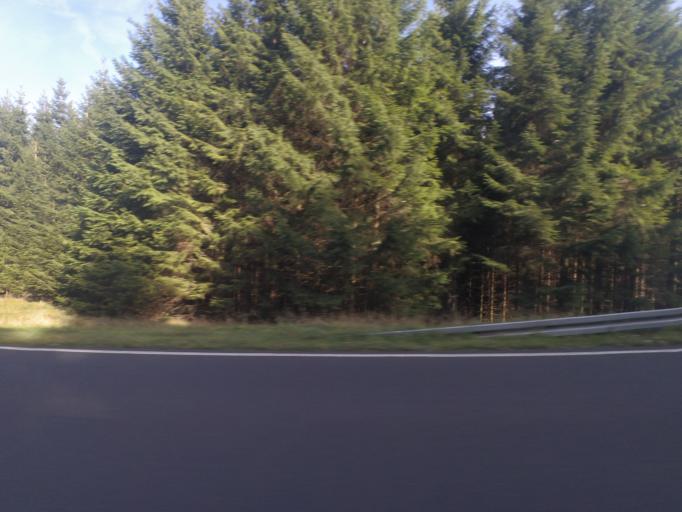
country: DE
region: Hesse
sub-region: Regierungsbezirk Kassel
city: Poppenhausen
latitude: 50.5233
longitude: 9.9063
